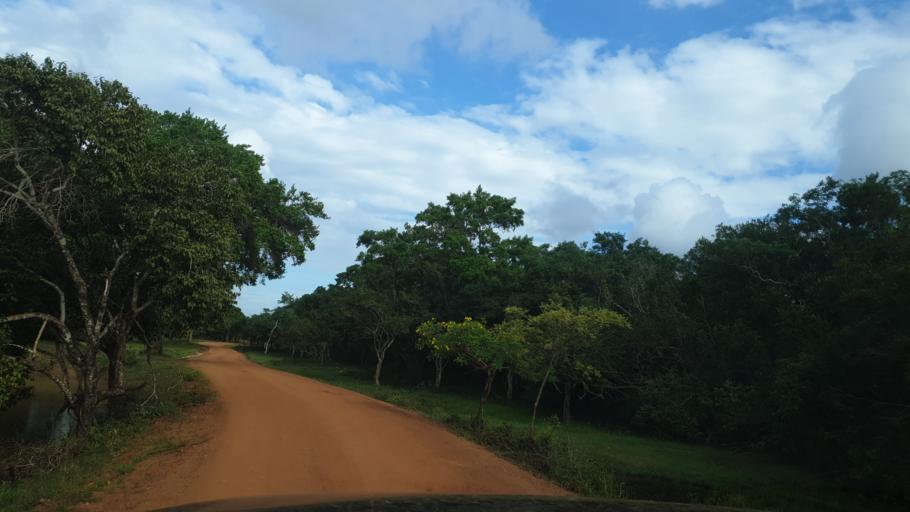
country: LK
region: North Central
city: Anuradhapura
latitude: 8.3634
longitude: 80.1005
